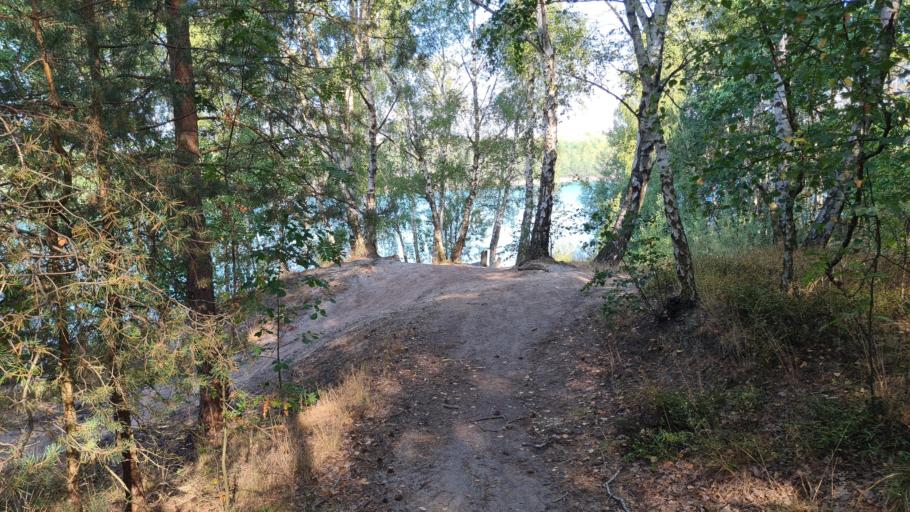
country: DE
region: Brandenburg
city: Sallgast
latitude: 51.5708
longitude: 13.8445
